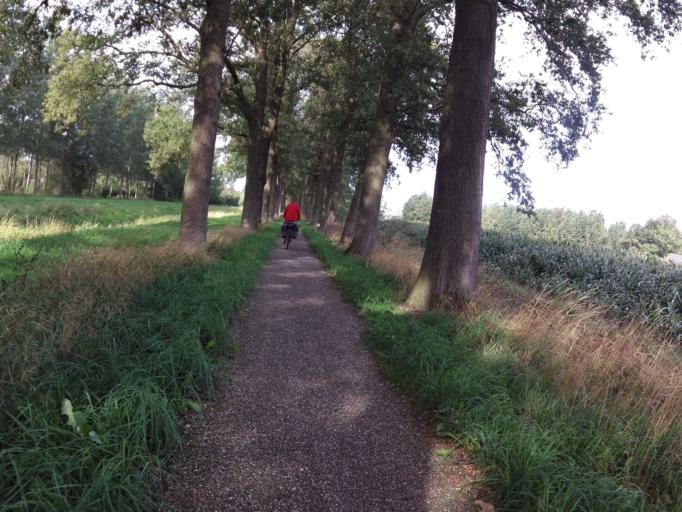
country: NL
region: Gelderland
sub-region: Oude IJsselstreek
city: Wisch
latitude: 51.9651
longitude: 6.4244
